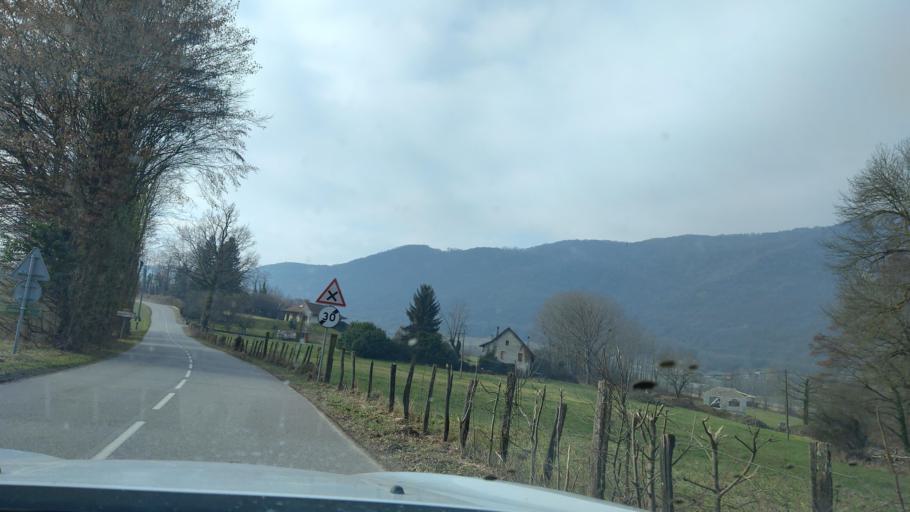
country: FR
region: Rhone-Alpes
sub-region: Departement de la Savoie
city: La Biolle
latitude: 45.7423
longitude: 5.9323
